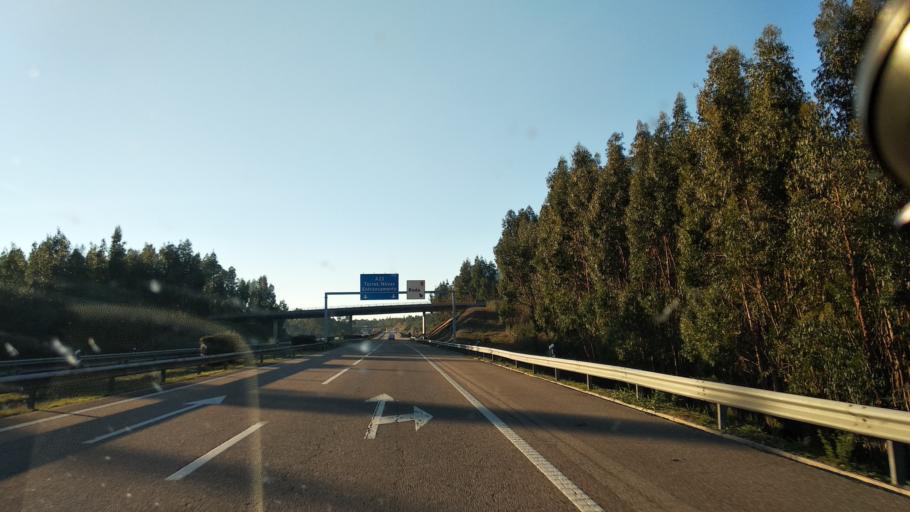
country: PT
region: Santarem
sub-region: Constancia
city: Constancia
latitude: 39.4866
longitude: -8.3846
